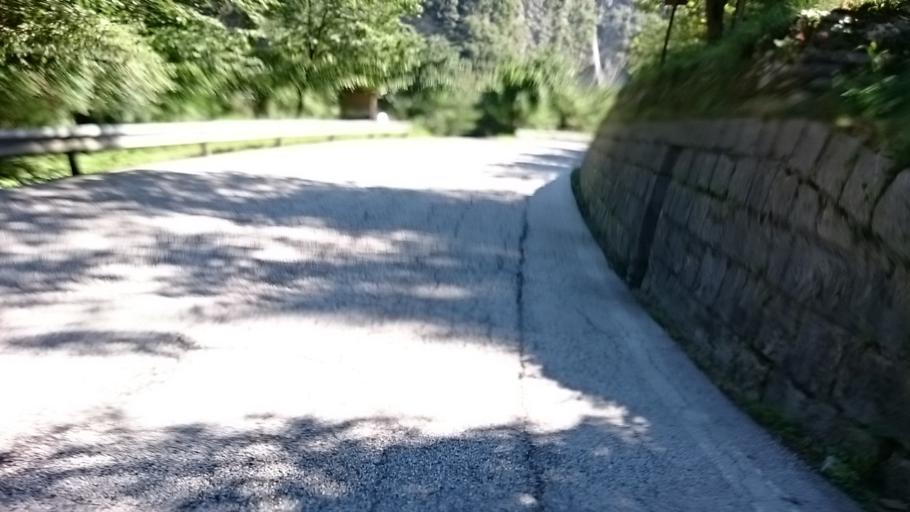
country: IT
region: Veneto
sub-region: Provincia di Belluno
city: Ospitale di Cadore
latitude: 46.3047
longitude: 12.3239
